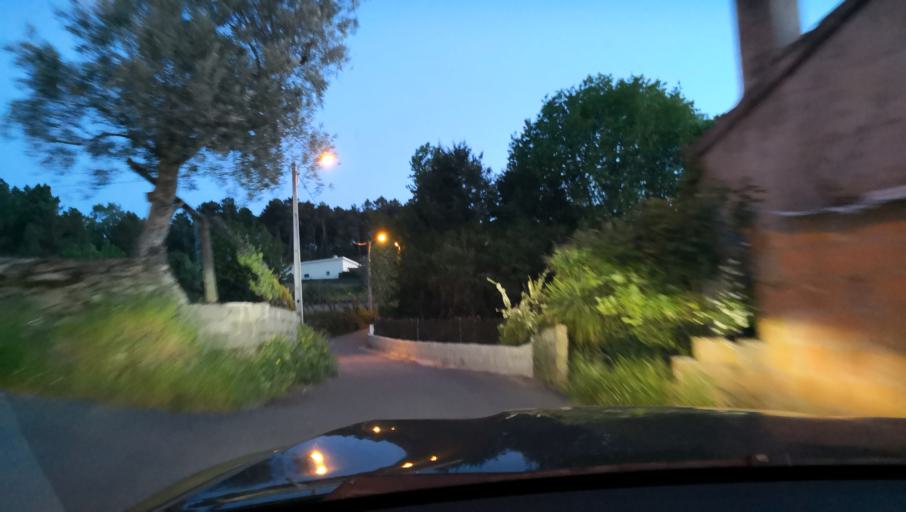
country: PT
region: Vila Real
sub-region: Vila Real
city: Vila Real
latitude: 41.3214
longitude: -7.6874
